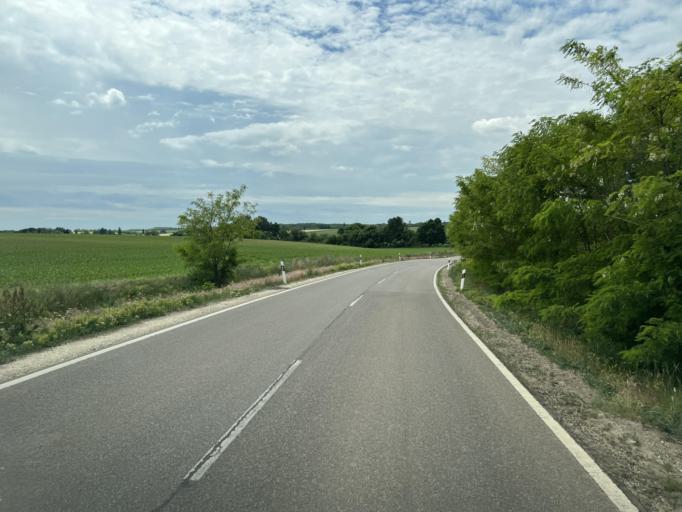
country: HU
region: Pest
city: Koka
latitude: 47.5077
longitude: 19.5953
